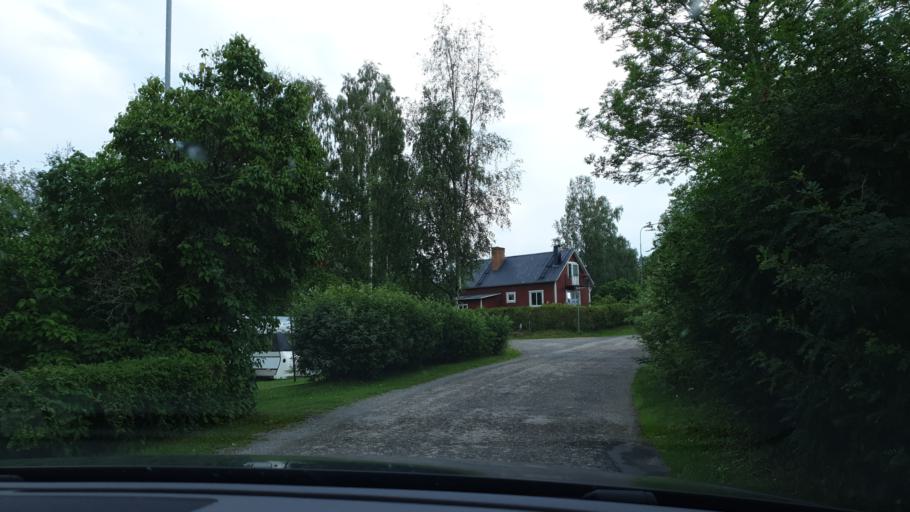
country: SE
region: Gaevleborg
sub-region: Hudiksvalls Kommun
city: Iggesund
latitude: 61.5422
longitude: 17.0056
